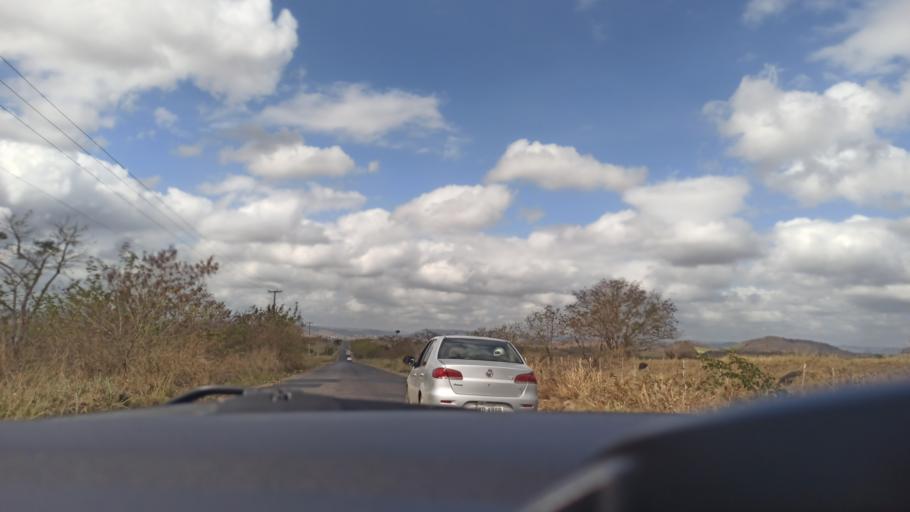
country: BR
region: Pernambuco
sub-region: Timbauba
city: Timbauba
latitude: -7.4735
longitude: -35.2779
